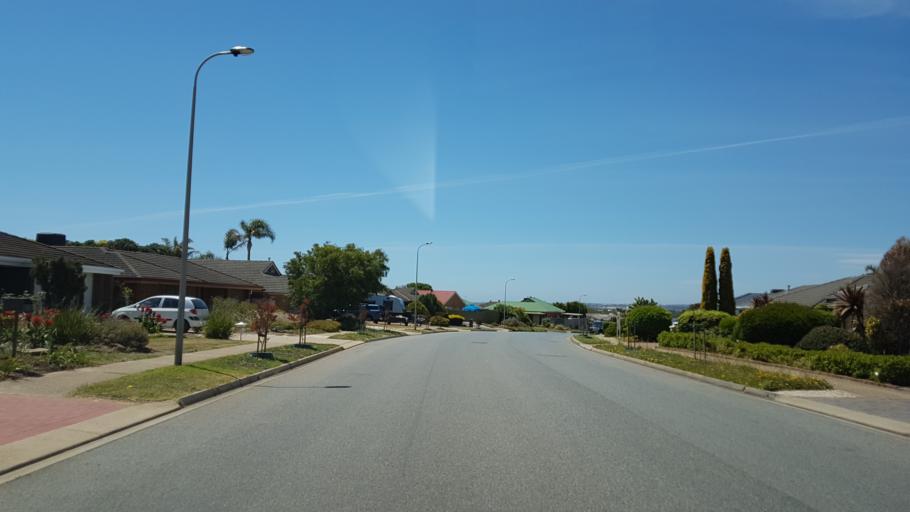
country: AU
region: South Australia
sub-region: Onkaparinga
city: Moana
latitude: -35.2154
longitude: 138.4749
